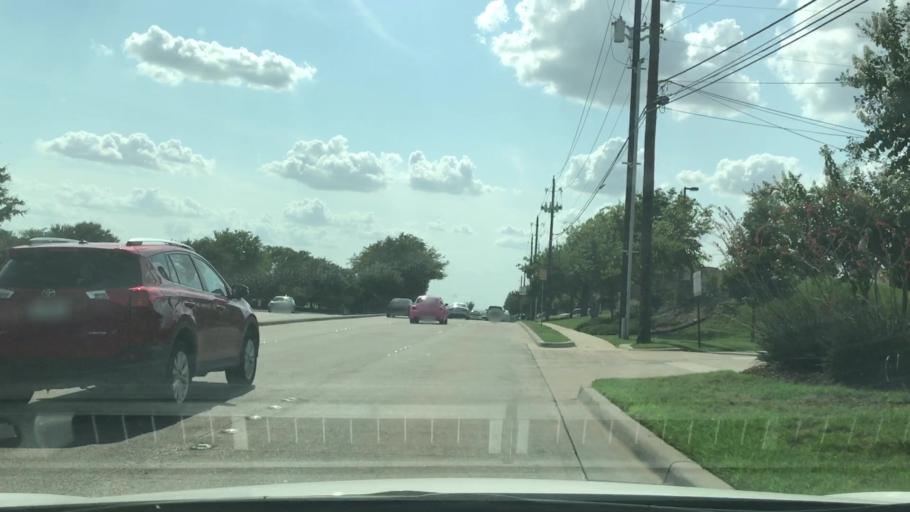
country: US
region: Texas
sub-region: Dallas County
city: Addison
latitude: 32.9703
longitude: -96.8563
